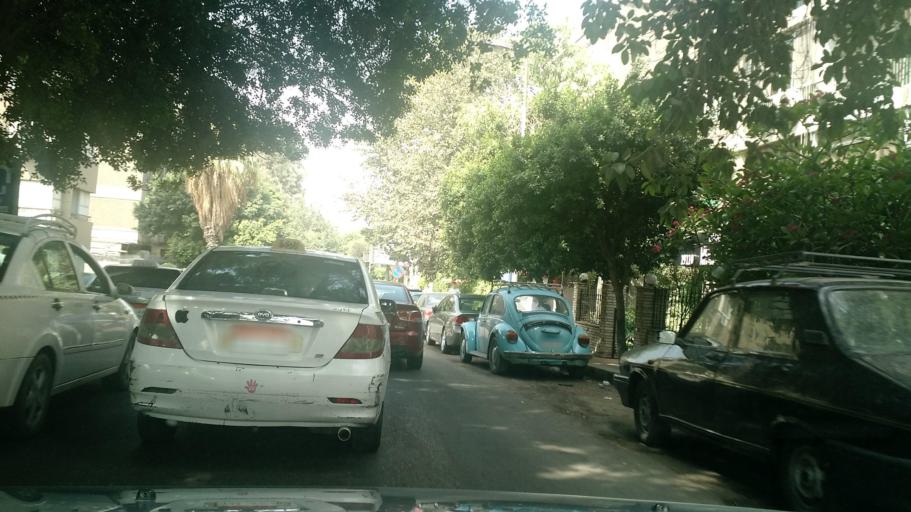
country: EG
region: Al Jizah
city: Al Hawamidiyah
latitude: 29.9643
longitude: 31.2758
